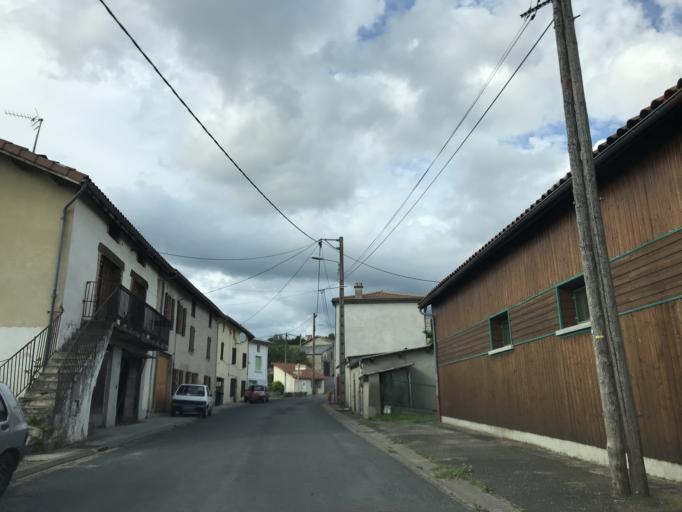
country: FR
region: Auvergne
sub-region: Departement du Puy-de-Dome
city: Celles-sur-Durolle
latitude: 45.8209
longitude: 3.6120
